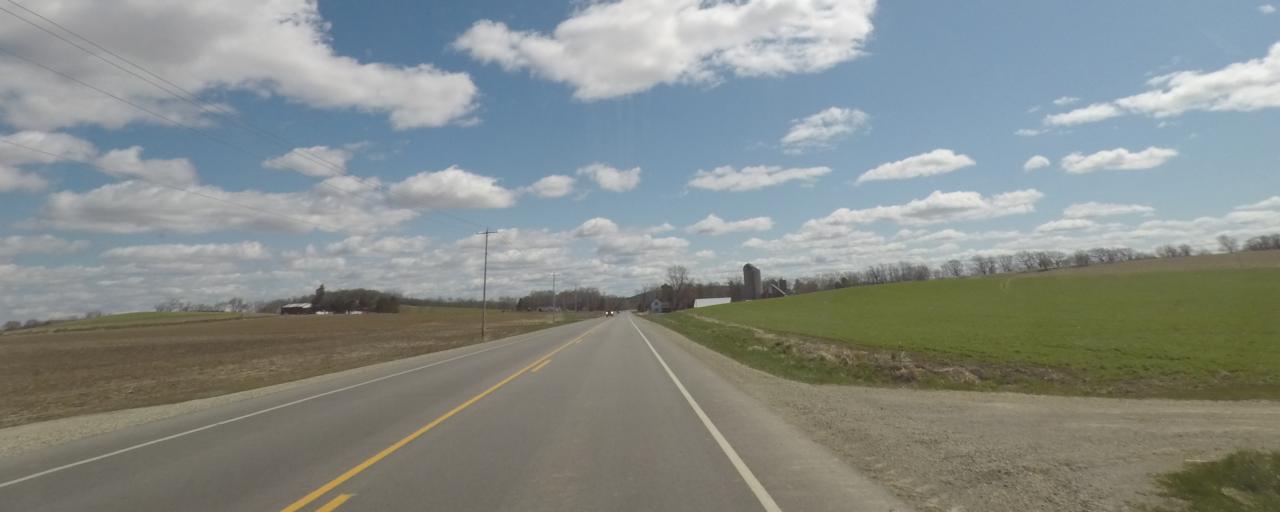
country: US
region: Wisconsin
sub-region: Jefferson County
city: Lake Mills
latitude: 43.0861
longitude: -88.9865
